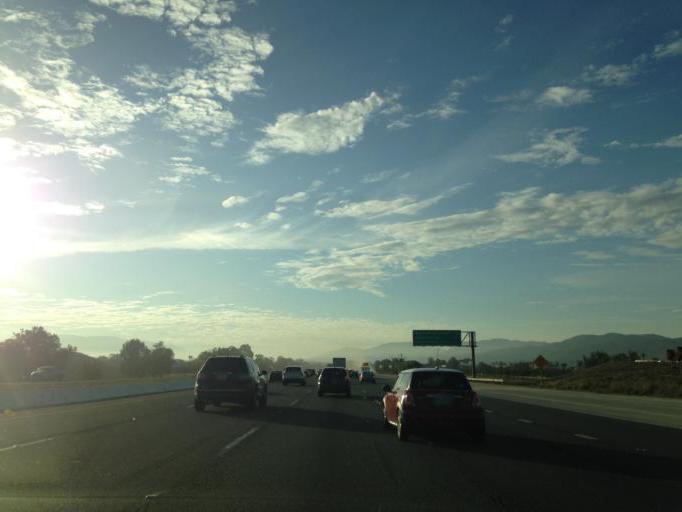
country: US
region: California
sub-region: Riverside County
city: Murrieta Hot Springs
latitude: 33.5322
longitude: -117.1696
